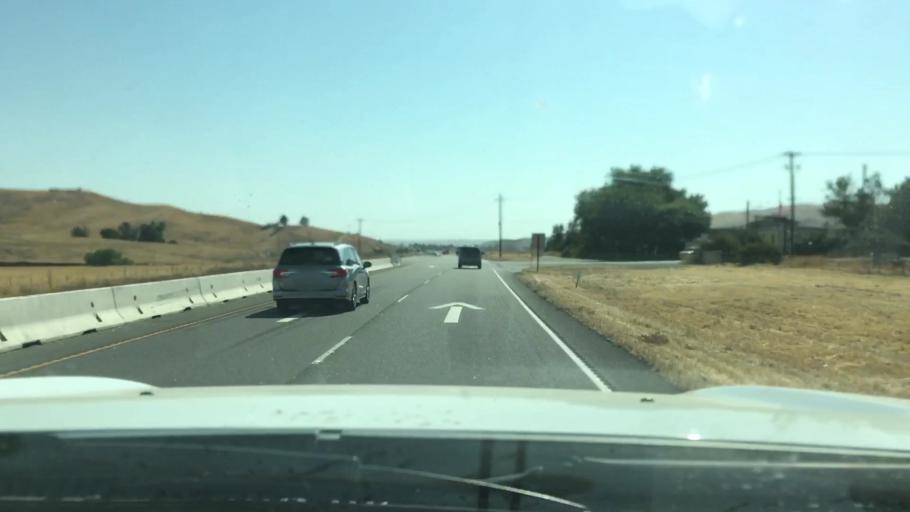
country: US
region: California
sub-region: San Luis Obispo County
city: Shandon
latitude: 35.7008
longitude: -120.3240
